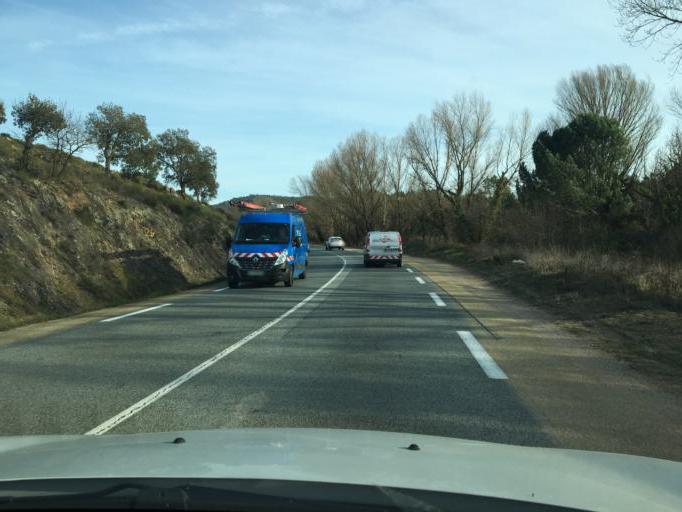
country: FR
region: Provence-Alpes-Cote d'Azur
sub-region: Departement du Var
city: Montauroux
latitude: 43.5500
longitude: 6.8000
